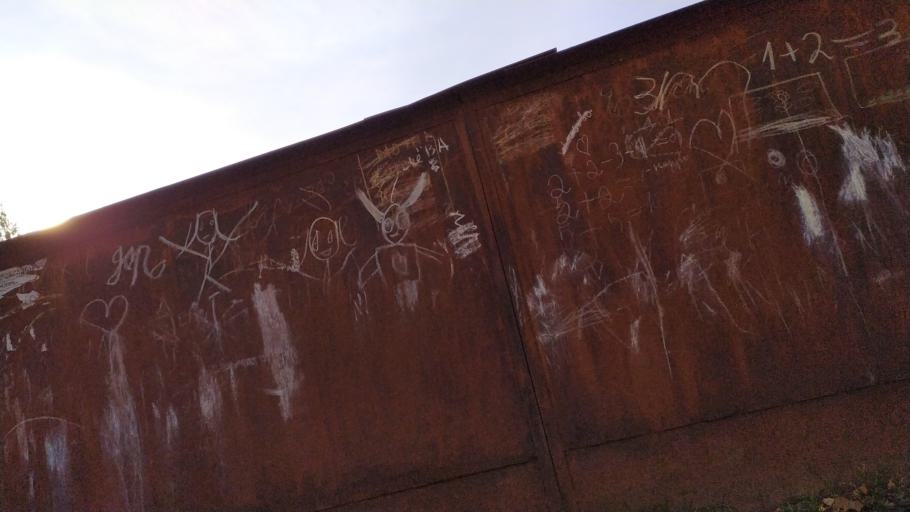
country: RU
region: Kursk
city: Kursk
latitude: 51.6483
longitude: 36.1388
